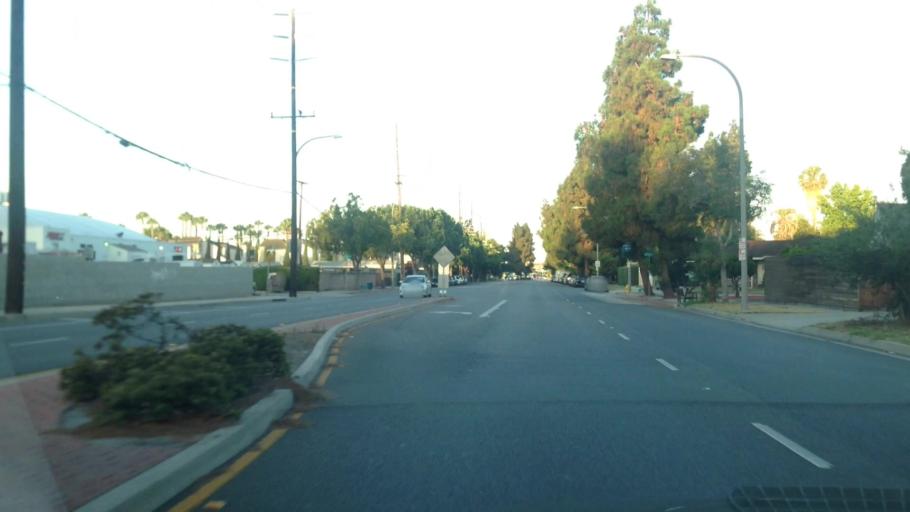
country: US
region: California
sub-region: Los Angeles County
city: Ladera Heights
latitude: 33.9930
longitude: -118.3910
